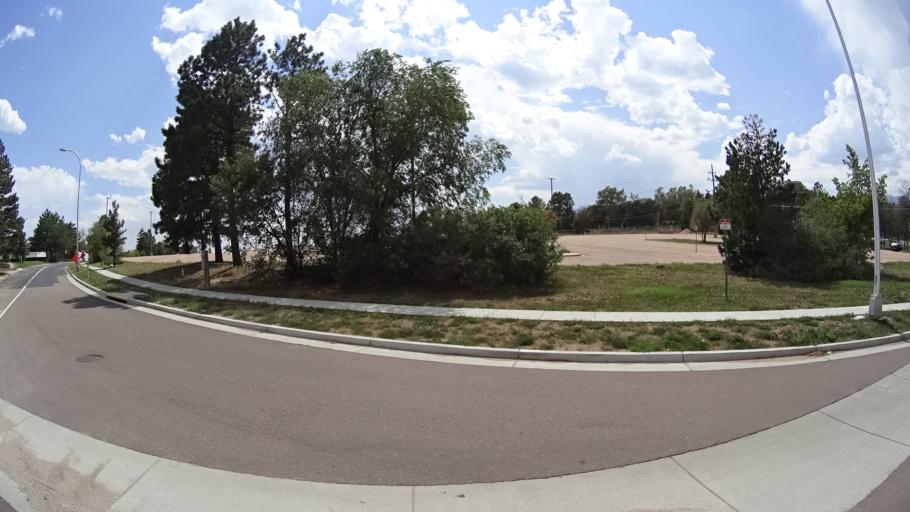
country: US
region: Colorado
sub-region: El Paso County
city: Colorado Springs
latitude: 38.8327
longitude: -104.7893
